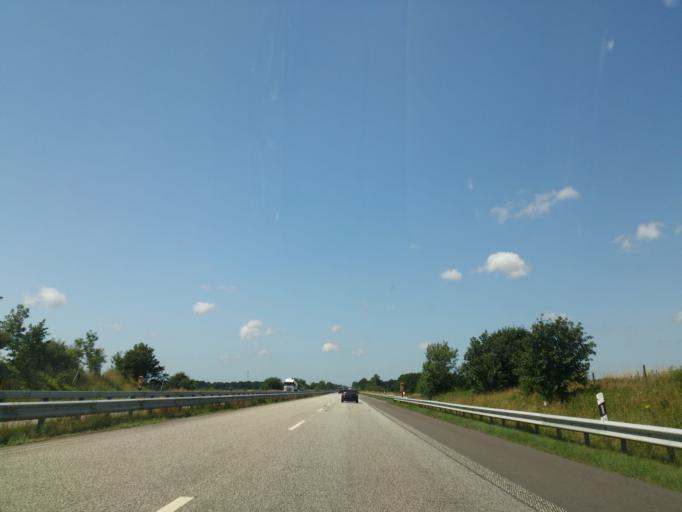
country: DE
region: Schleswig-Holstein
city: Nordhastedt
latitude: 54.1640
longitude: 9.1876
